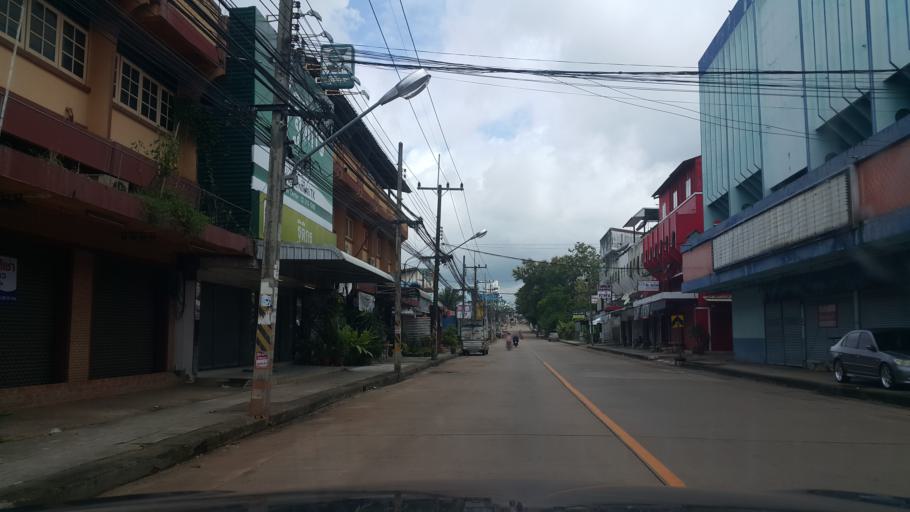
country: TH
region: Uttaradit
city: Uttaradit
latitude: 17.6143
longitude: 100.0895
